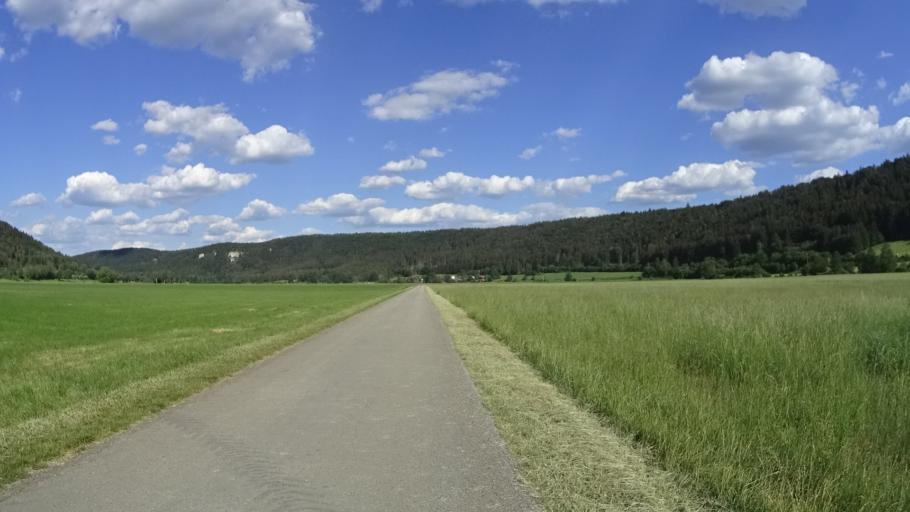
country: DE
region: Bavaria
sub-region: Upper Palatinate
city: Dietfurt
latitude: 49.0130
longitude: 11.5347
